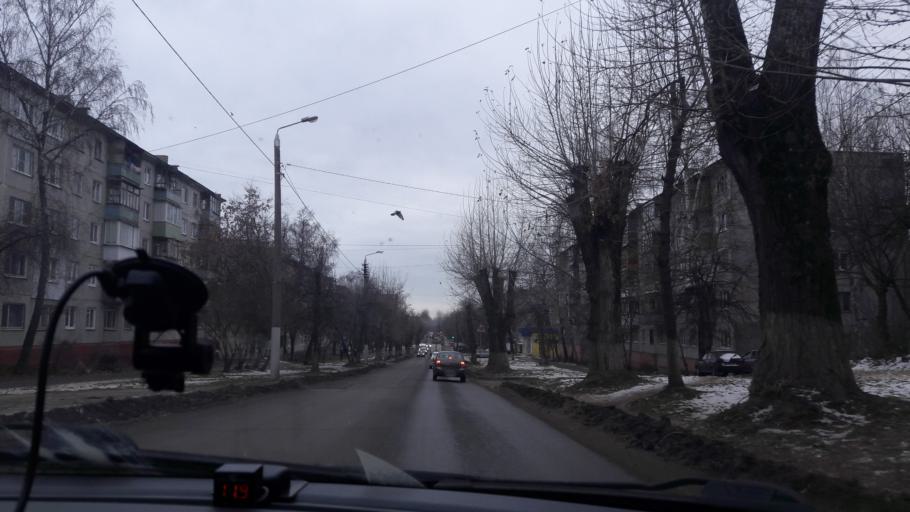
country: RU
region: Tula
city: Tula
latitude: 54.2022
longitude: 37.6578
